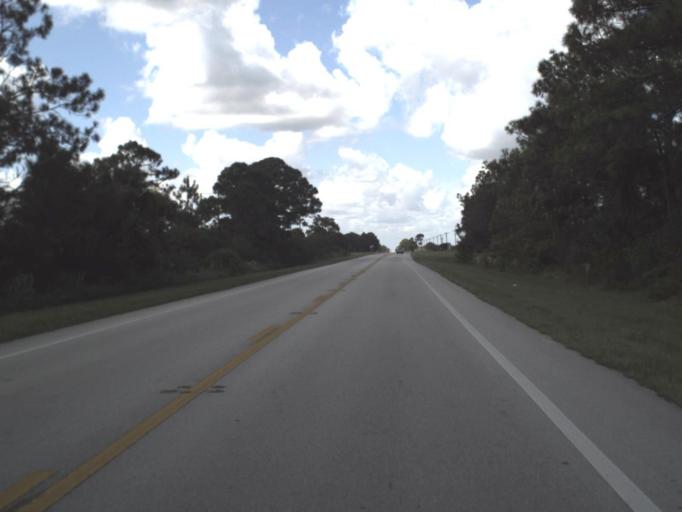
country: US
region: Florida
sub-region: Lee County
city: Lehigh Acres
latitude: 26.5122
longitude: -81.5391
